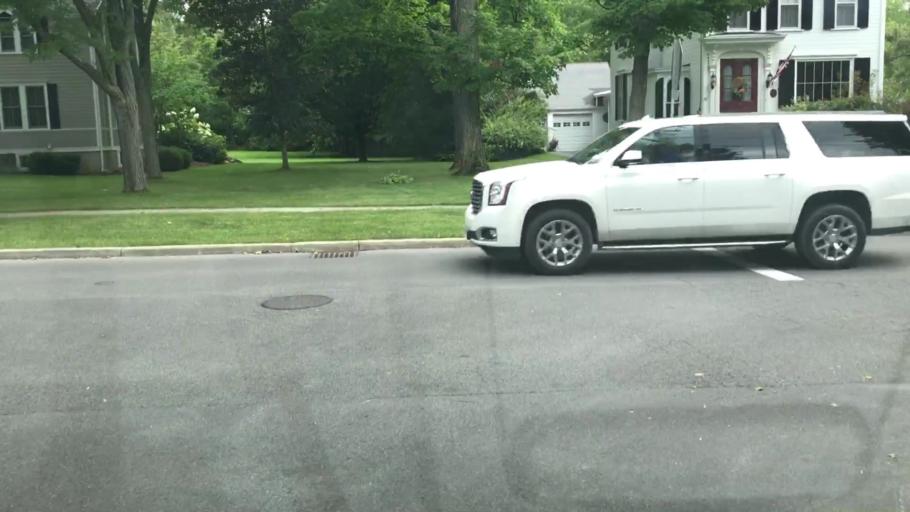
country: US
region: New York
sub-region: Onondaga County
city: Skaneateles
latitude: 42.9478
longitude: -76.4235
